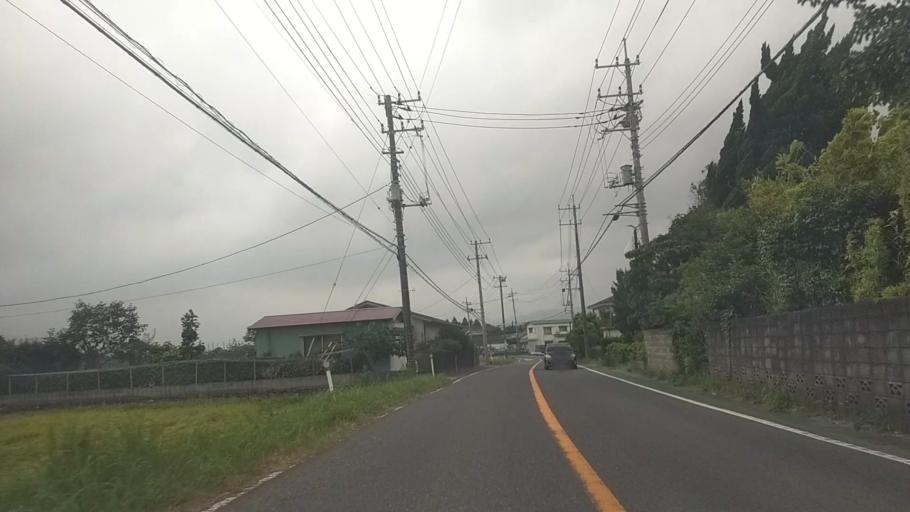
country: JP
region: Chiba
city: Kawaguchi
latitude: 35.1268
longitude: 140.0556
